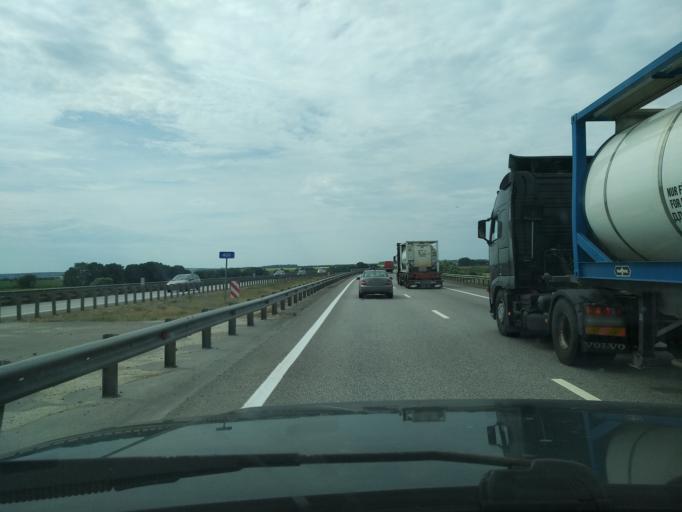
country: RU
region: Lipetsk
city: Khlevnoye
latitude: 52.0578
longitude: 39.1887
